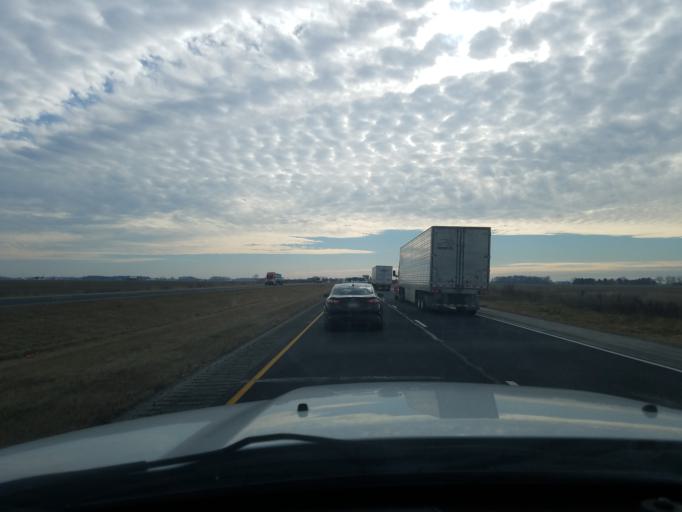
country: US
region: Indiana
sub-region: Huntington County
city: Markle
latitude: 40.8850
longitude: -85.3454
